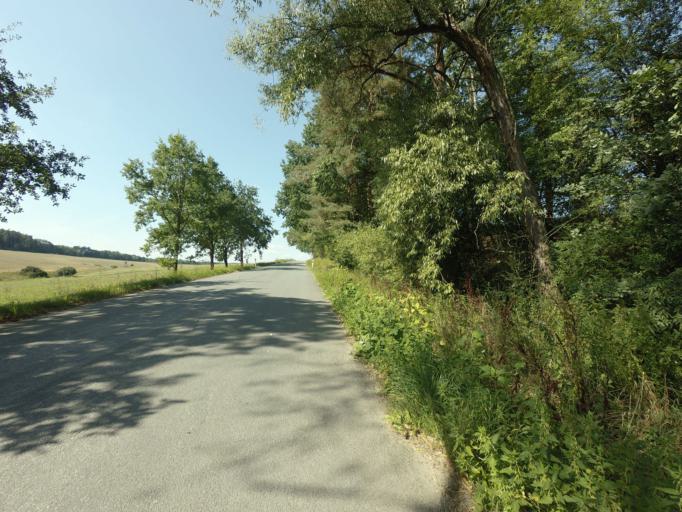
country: CZ
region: Jihocesky
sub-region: Okres Ceske Budejovice
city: Hluboka nad Vltavou
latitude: 49.1393
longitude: 14.4481
